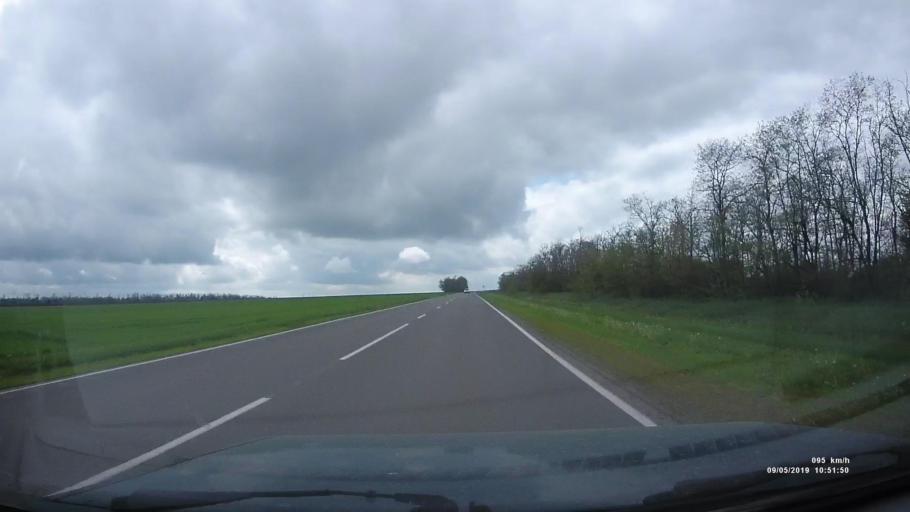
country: RU
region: Rostov
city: Peshkovo
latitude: 46.9087
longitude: 39.3542
